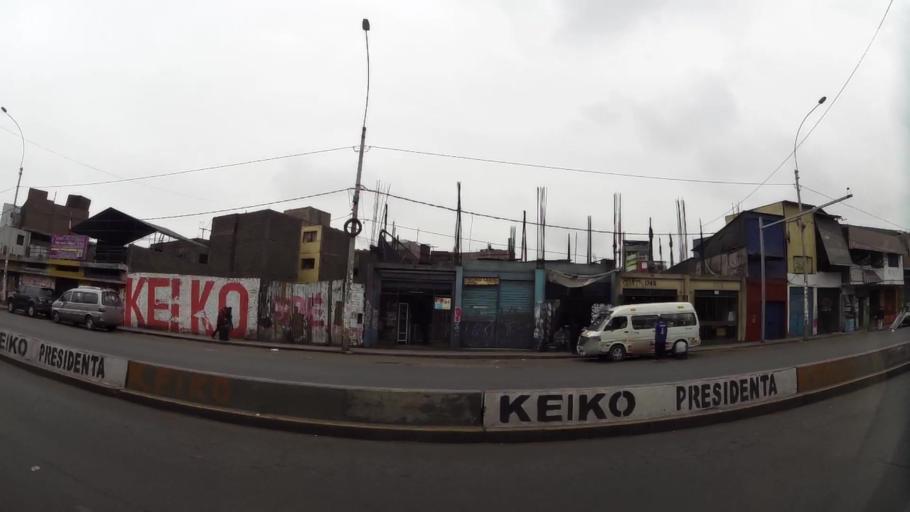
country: PE
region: Lima
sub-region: Lima
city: San Luis
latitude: -12.0713
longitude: -77.0109
